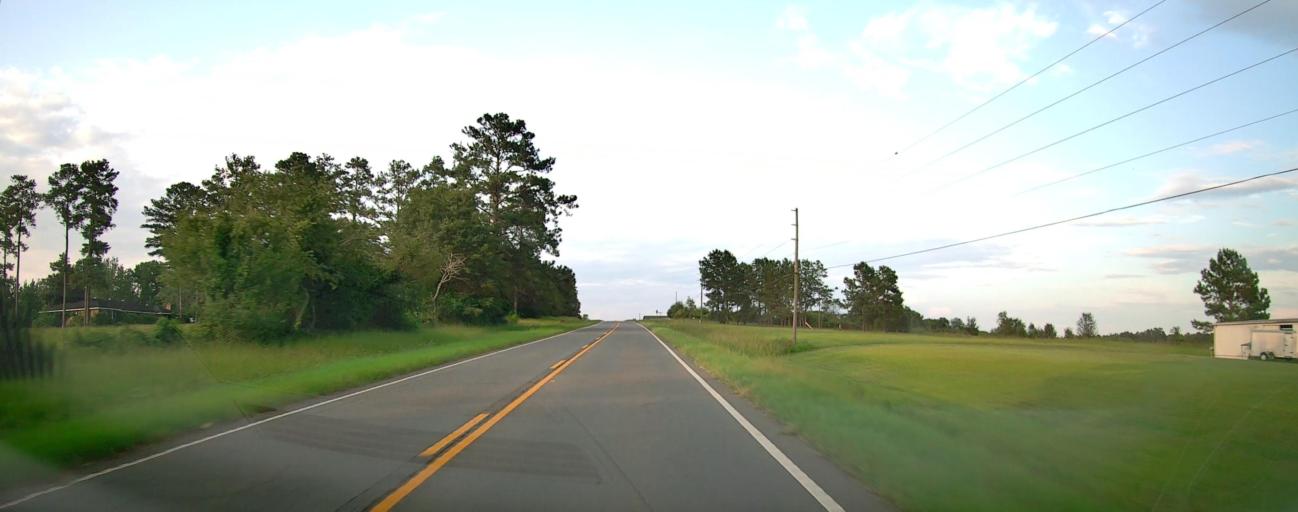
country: US
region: Georgia
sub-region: Crawford County
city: Roberta
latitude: 32.6735
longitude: -84.0923
